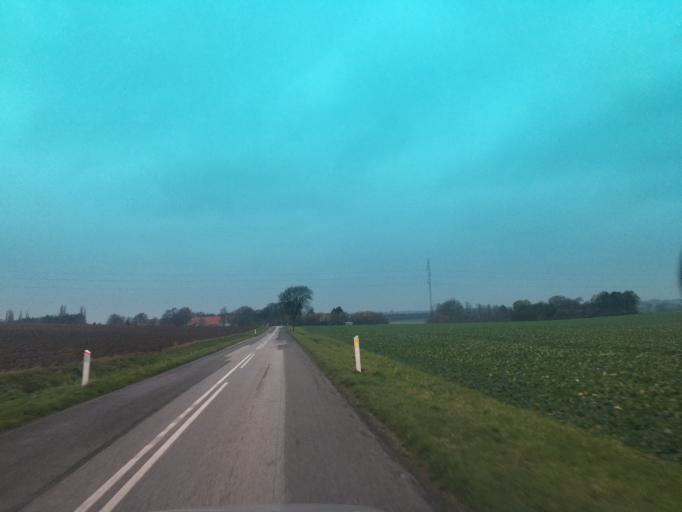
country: DK
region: Zealand
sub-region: Slagelse Kommune
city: Skaelskor
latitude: 55.2607
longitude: 11.4177
